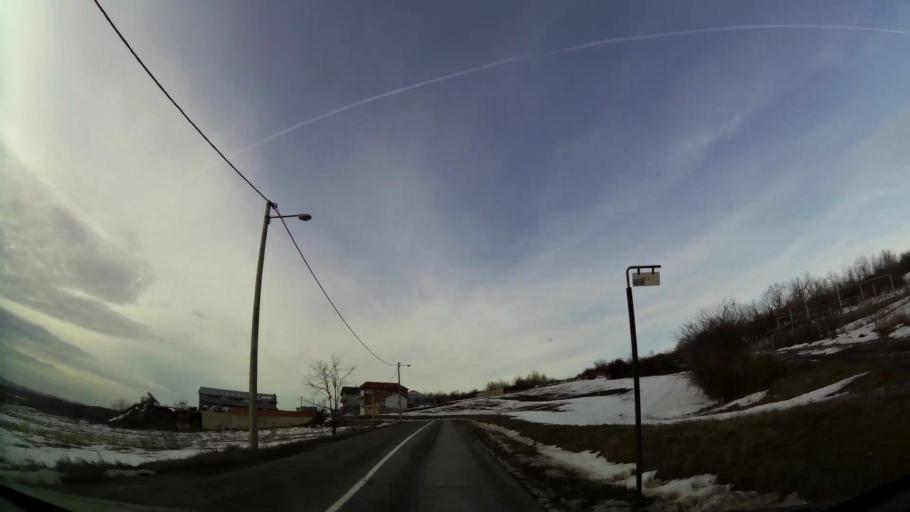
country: RS
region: Central Serbia
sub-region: Belgrade
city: Zvezdara
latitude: 44.7253
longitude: 20.5077
